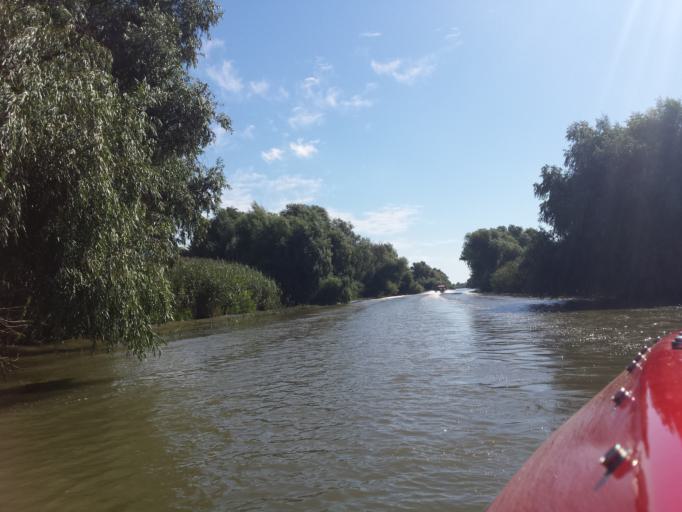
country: RO
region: Tulcea
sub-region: Comuna Mahmudia
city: Mahmudia
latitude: 45.2391
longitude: 29.1255
